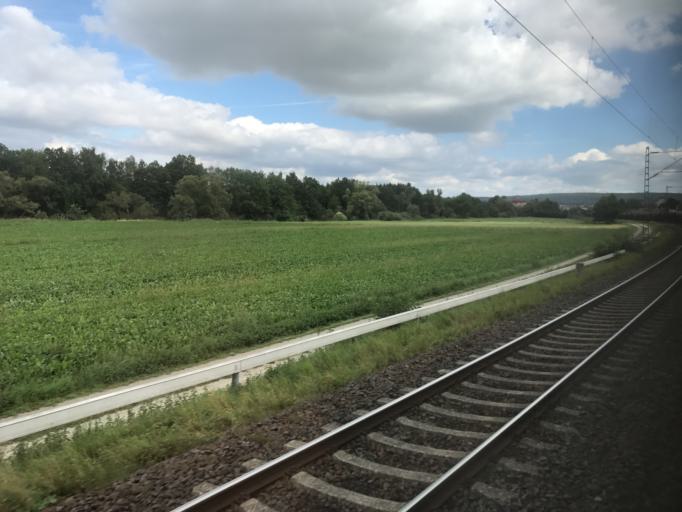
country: DE
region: Hesse
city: Felsberg
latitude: 51.1221
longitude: 9.4271
